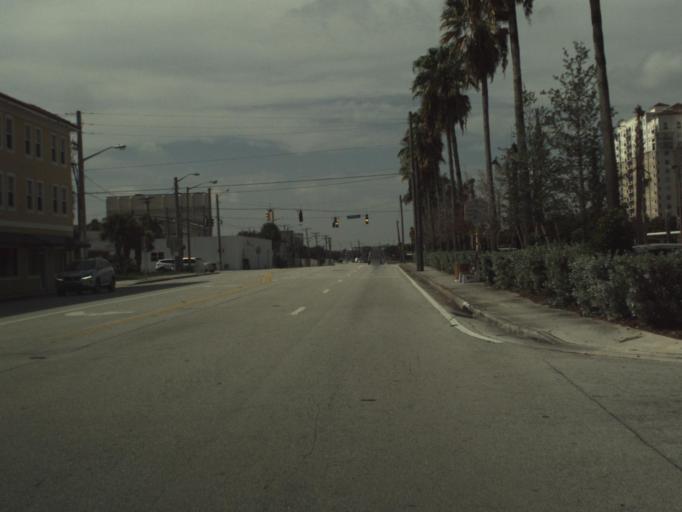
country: US
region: Florida
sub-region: Palm Beach County
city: West Palm Beach
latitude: 26.7116
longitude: -80.0621
